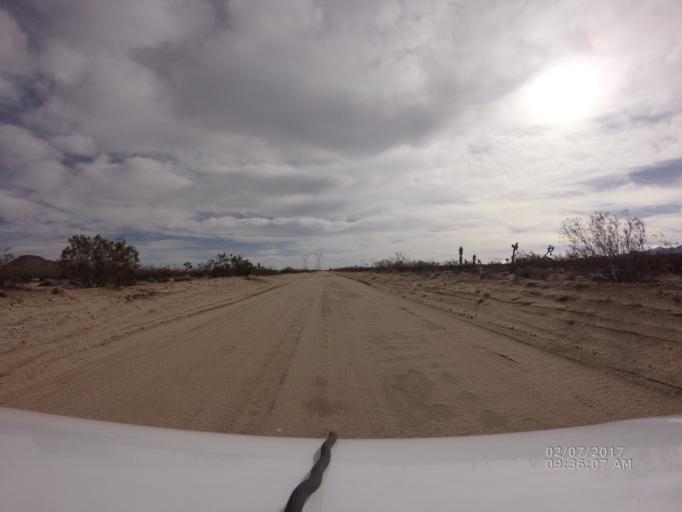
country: US
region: California
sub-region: San Bernardino County
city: Pinon Hills
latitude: 34.5276
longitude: -117.7165
